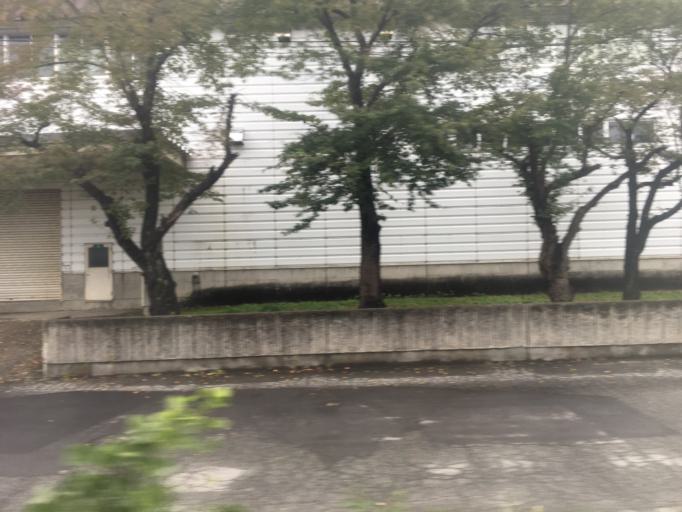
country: JP
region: Yamagata
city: Nagai
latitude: 38.0643
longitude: 139.7478
